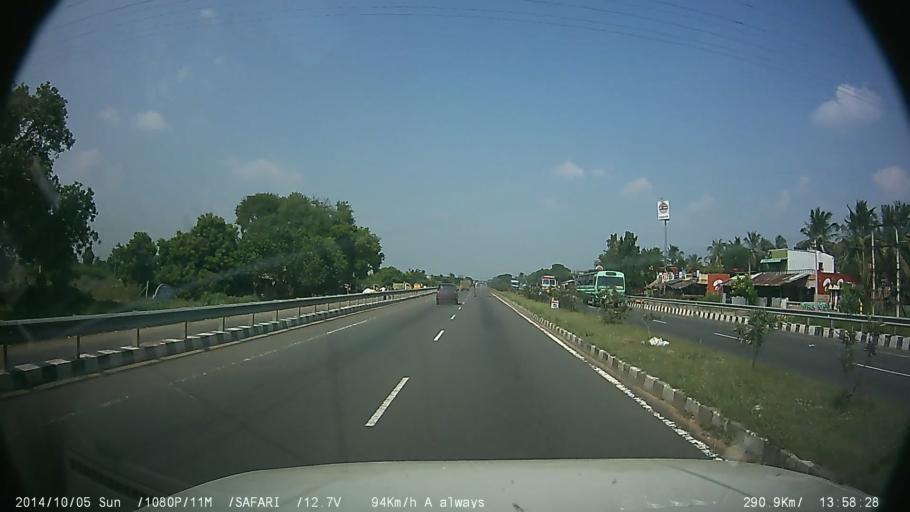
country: IN
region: Tamil Nadu
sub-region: Villupuram
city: Tindivanam
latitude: 12.1589
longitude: 79.6089
